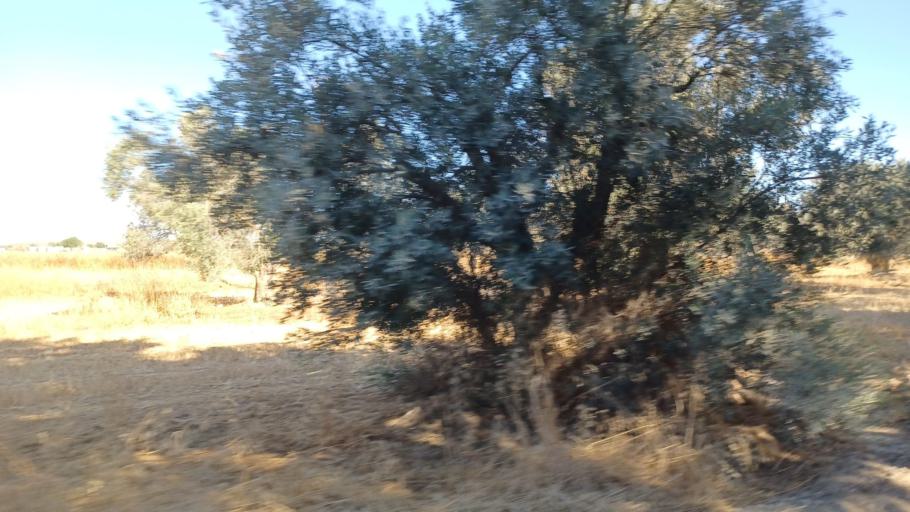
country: CY
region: Larnaka
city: Pergamos
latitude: 35.0463
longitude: 33.7044
